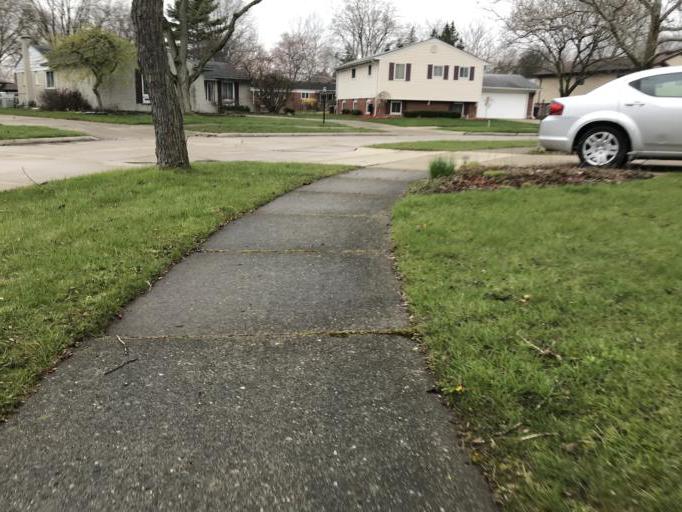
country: US
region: Michigan
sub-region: Oakland County
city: Farmington
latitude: 42.4685
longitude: -83.3428
